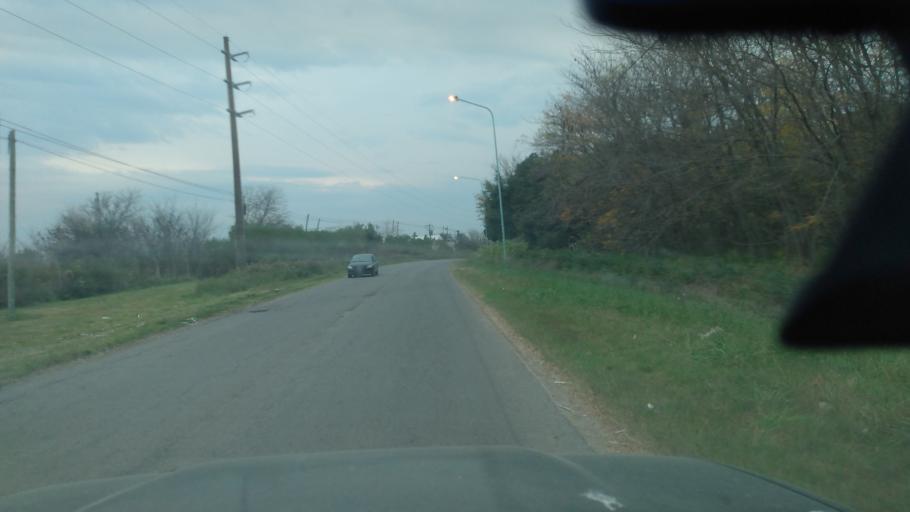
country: AR
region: Buenos Aires
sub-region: Partido de Lujan
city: Lujan
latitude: -34.5652
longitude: -59.1429
